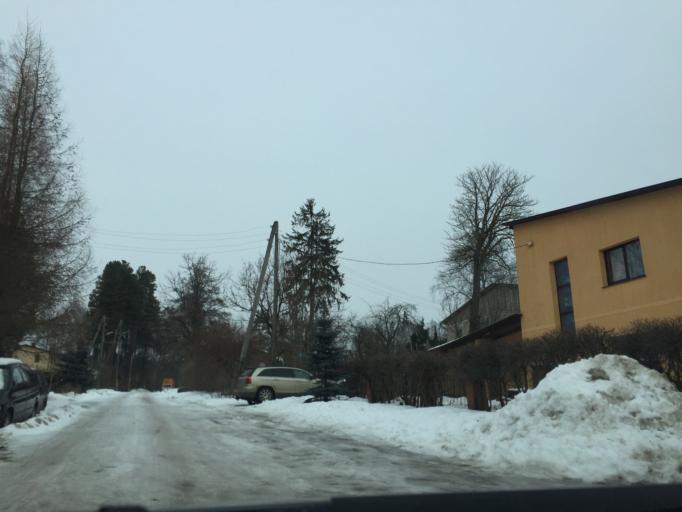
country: LV
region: Ogre
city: Ogre
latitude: 56.8207
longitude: 24.5751
